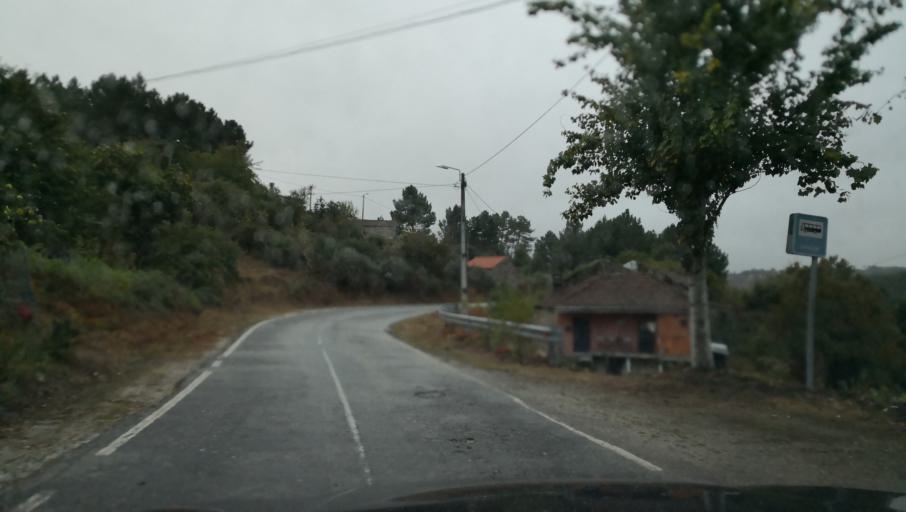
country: PT
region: Vila Real
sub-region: Sabrosa
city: Sabrosa
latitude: 41.3514
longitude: -7.5859
